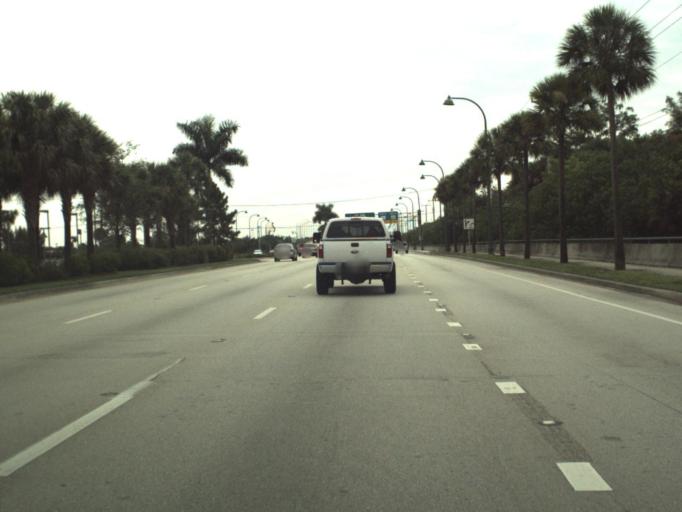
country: US
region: Florida
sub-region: Palm Beach County
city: Royal Palm Beach
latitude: 26.6805
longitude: -80.2118
